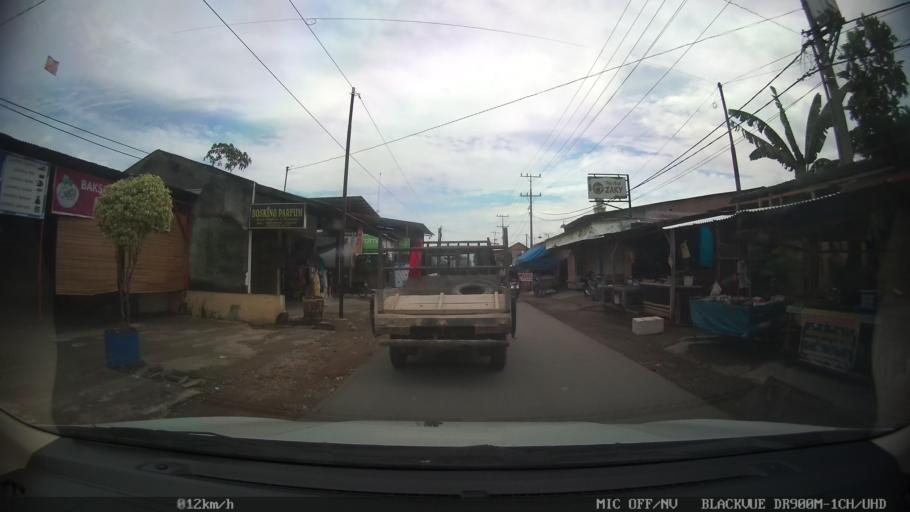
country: ID
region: North Sumatra
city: Sunggal
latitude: 3.6090
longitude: 98.5802
